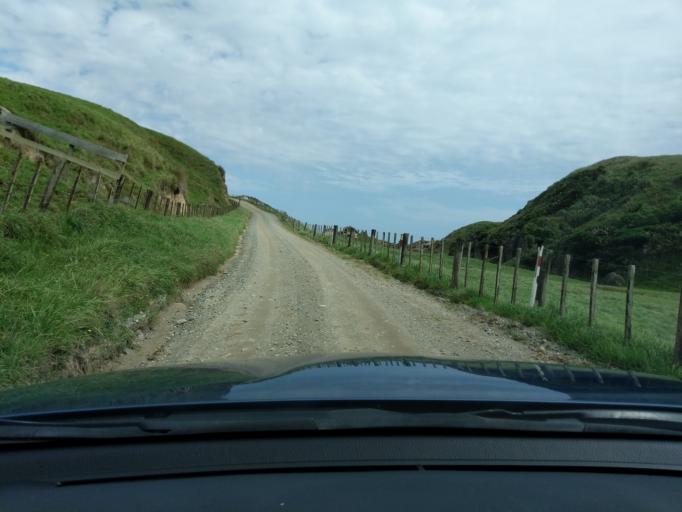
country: NZ
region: Tasman
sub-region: Tasman District
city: Takaka
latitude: -40.6528
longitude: 172.4196
